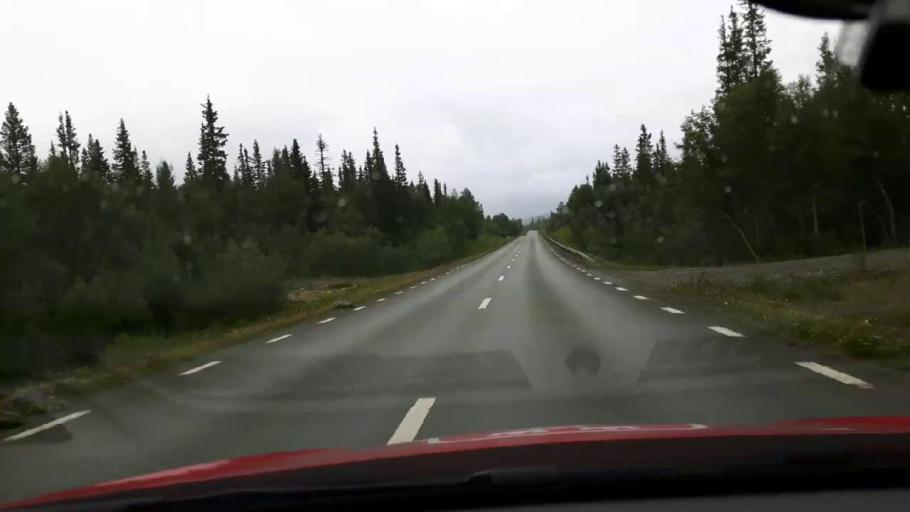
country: NO
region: Nord-Trondelag
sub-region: Meraker
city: Meraker
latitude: 63.2698
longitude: 12.1538
